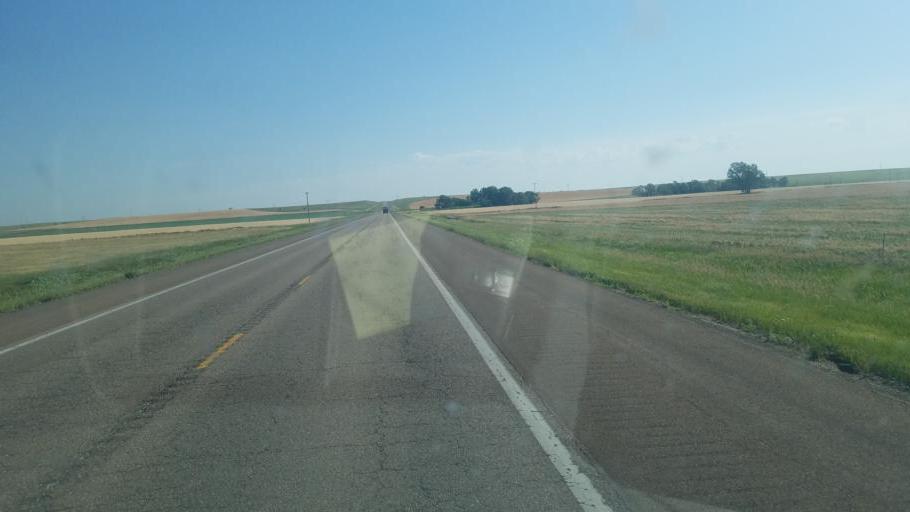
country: US
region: Kansas
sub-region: Barton County
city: Great Bend
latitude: 38.3744
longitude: -98.6887
